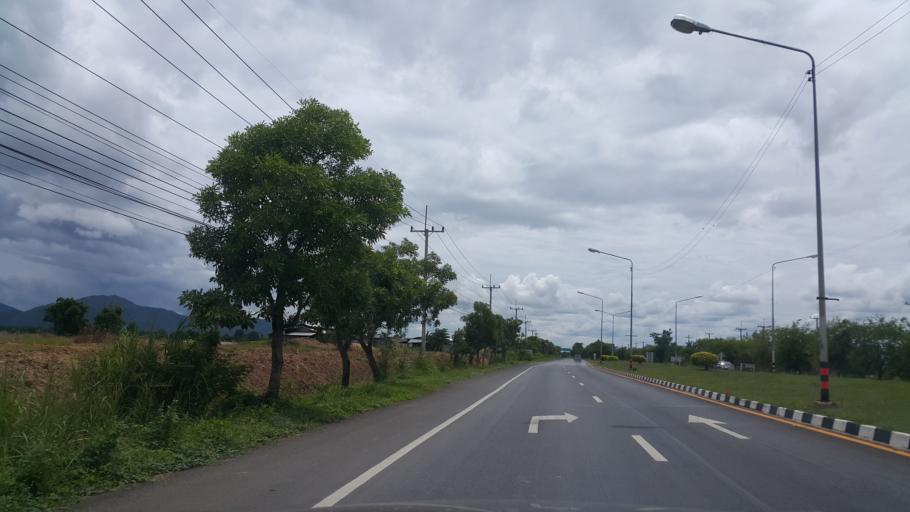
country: TH
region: Sukhothai
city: Ban Na
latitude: 17.0575
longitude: 99.7135
